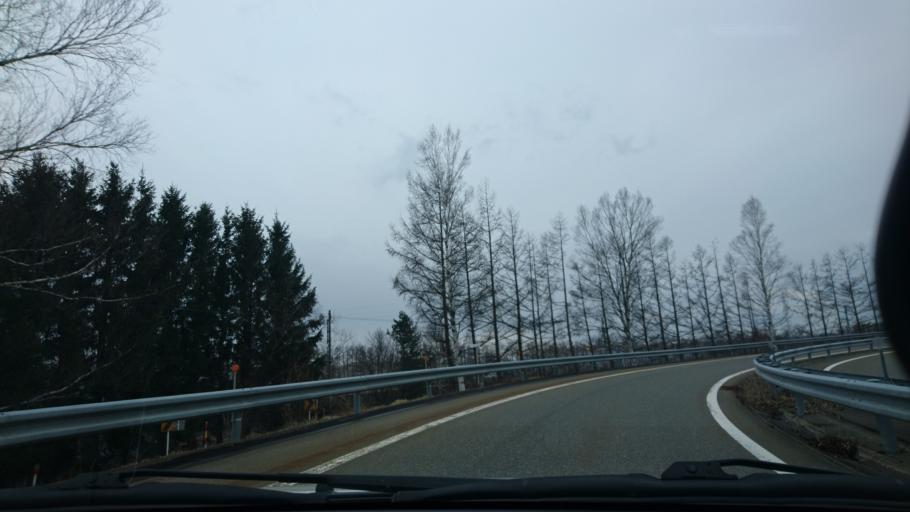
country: JP
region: Hokkaido
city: Otofuke
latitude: 42.9799
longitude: 143.1795
